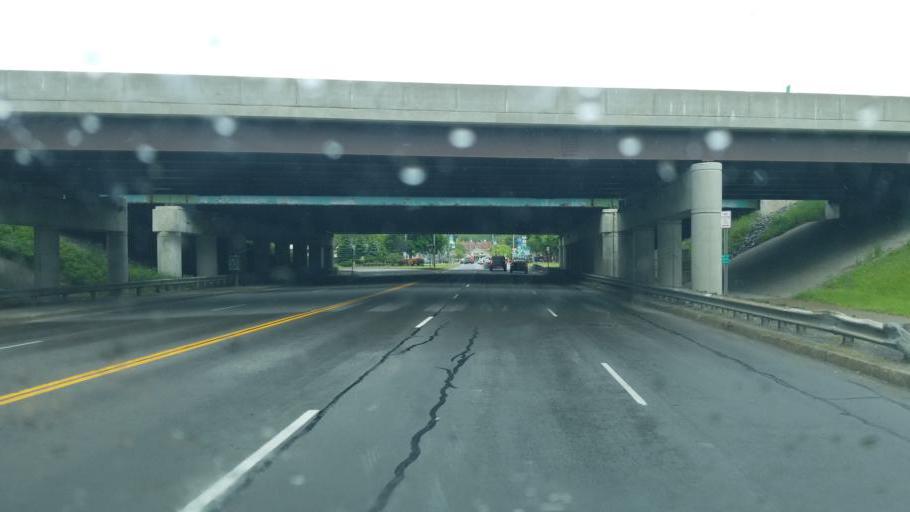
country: US
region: New York
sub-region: Oneida County
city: Utica
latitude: 43.1145
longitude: -75.2128
